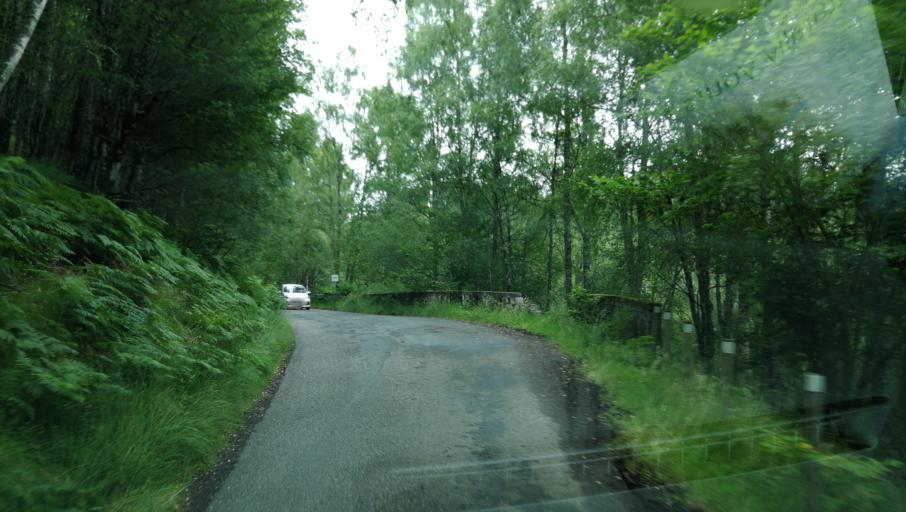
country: GB
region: Scotland
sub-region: Highland
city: Beauly
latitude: 57.3149
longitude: -4.8397
